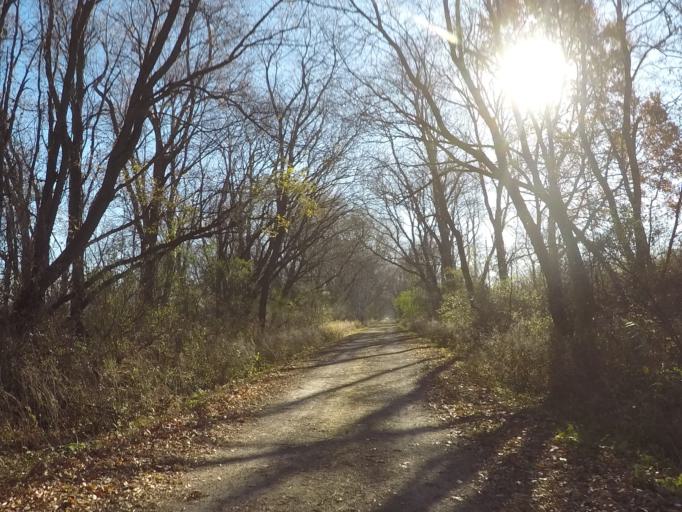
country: US
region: Wisconsin
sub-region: Dane County
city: Deerfield
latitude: 43.0485
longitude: -89.0592
